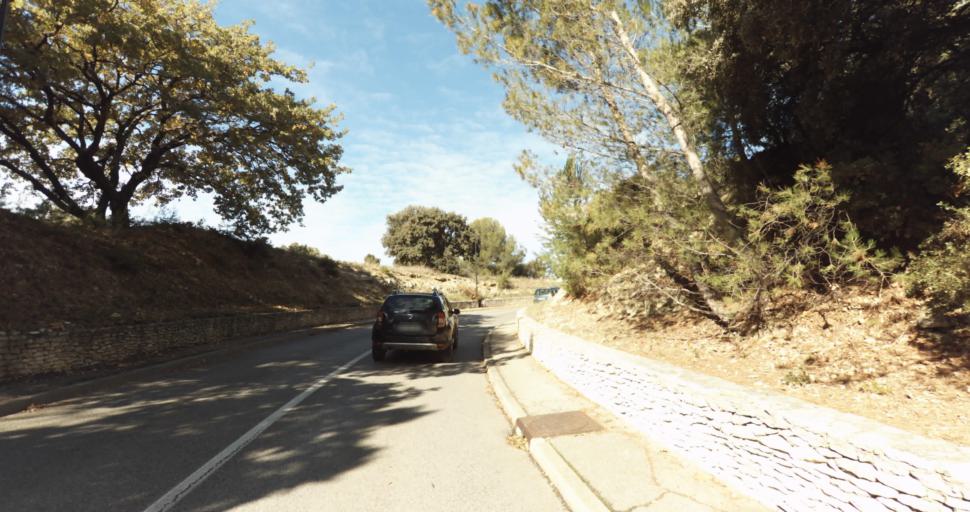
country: FR
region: Provence-Alpes-Cote d'Azur
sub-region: Departement des Bouches-du-Rhone
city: Venelles
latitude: 43.5875
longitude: 5.4739
